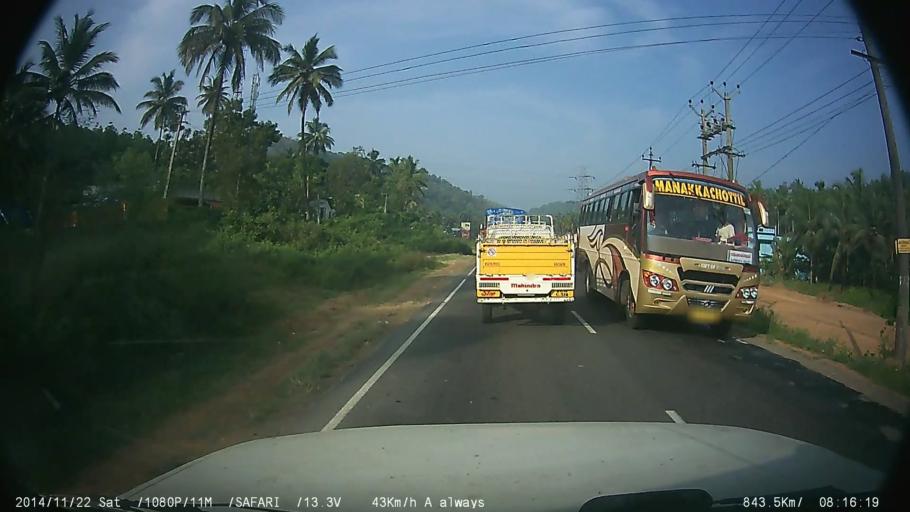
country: IN
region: Kerala
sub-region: Thrissur District
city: Chelakara
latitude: 10.5768
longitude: 76.4046
